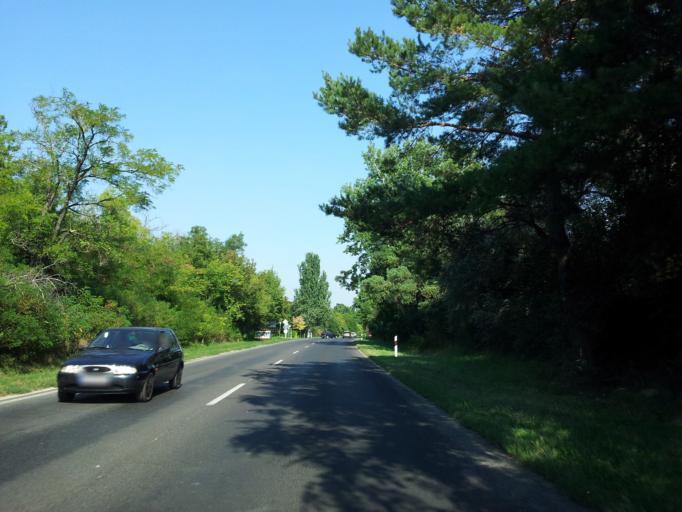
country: HU
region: Somogy
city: Balatonszabadi
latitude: 46.9277
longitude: 18.1185
